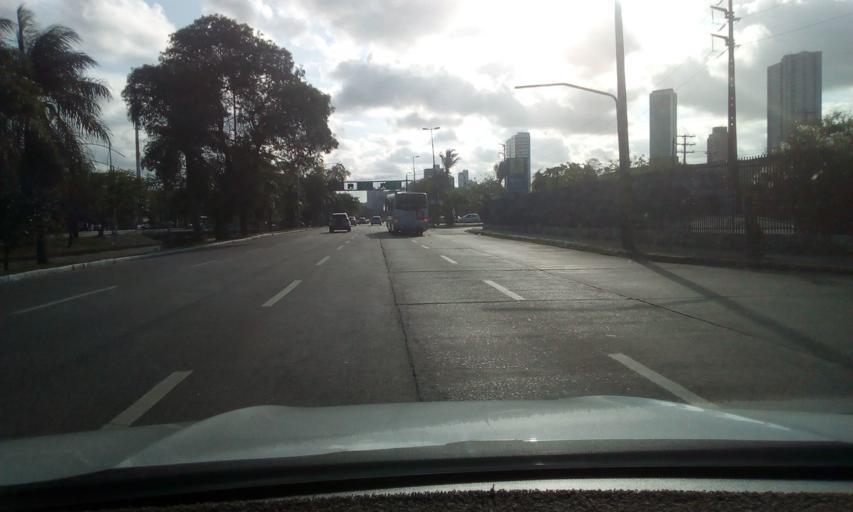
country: BR
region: Pernambuco
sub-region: Recife
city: Recife
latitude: -8.0391
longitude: -34.8780
